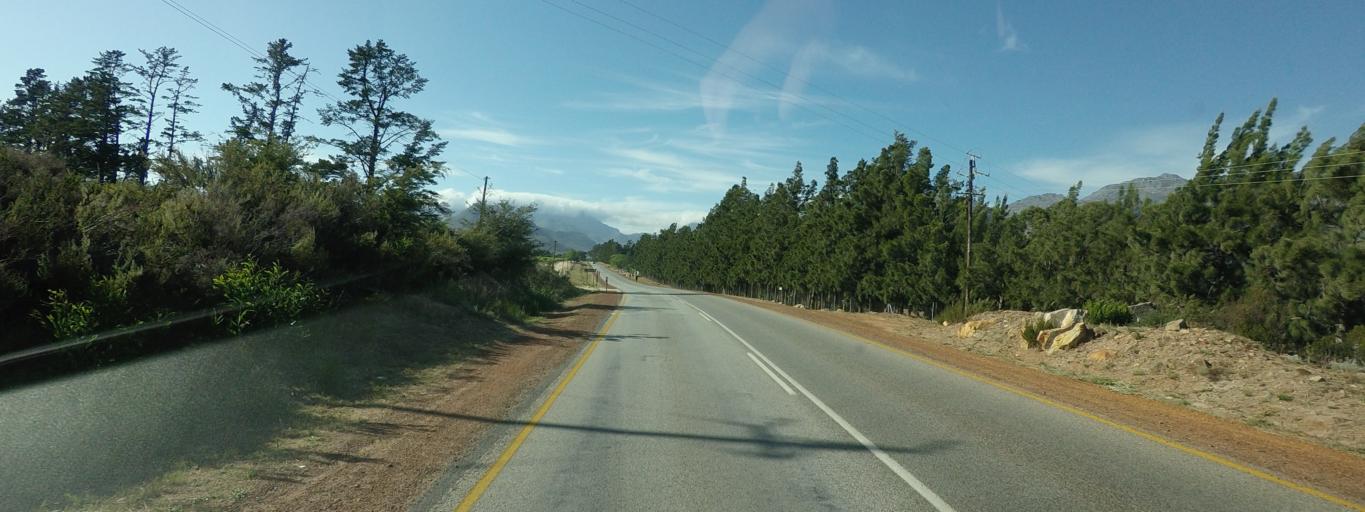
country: ZA
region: Western Cape
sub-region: Cape Winelands District Municipality
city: Paarl
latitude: -33.8632
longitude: 19.0397
